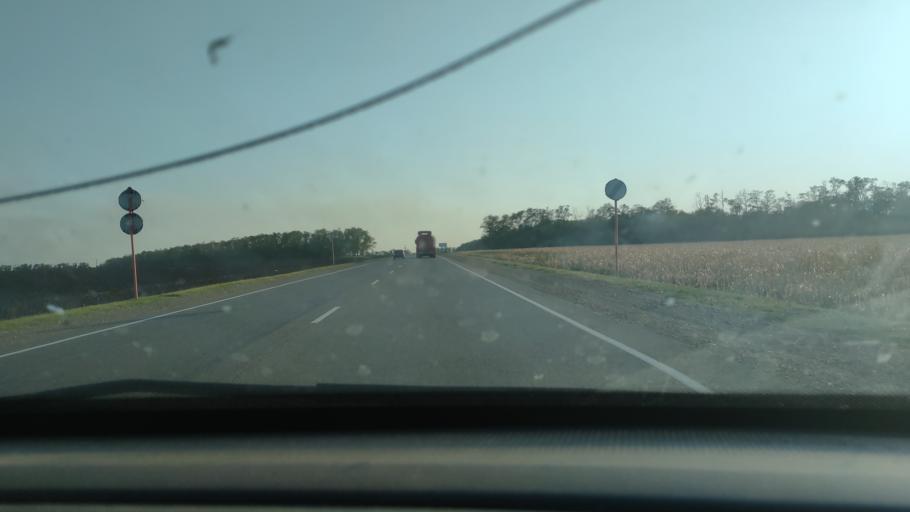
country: RU
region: Krasnodarskiy
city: Kanevskaya
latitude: 46.0413
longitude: 38.9862
